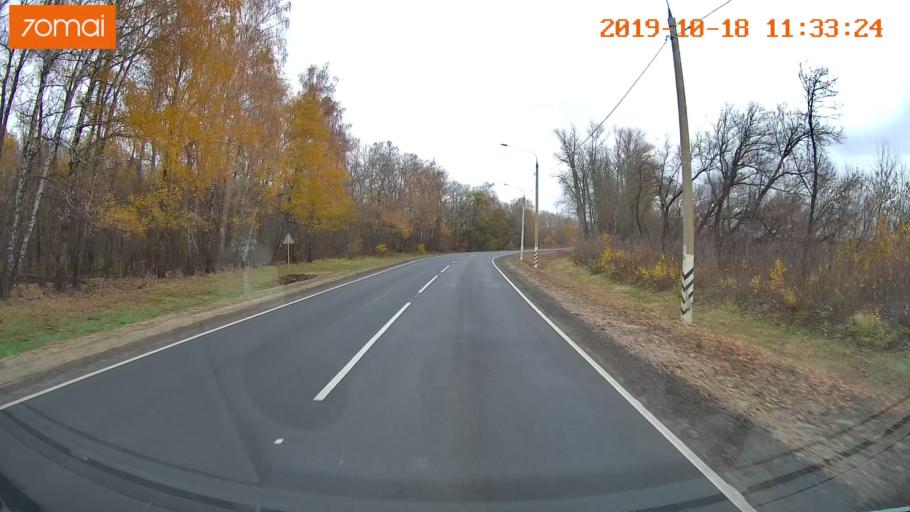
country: RU
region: Rjazan
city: Oktyabr'skiy
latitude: 54.1412
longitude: 38.7396
